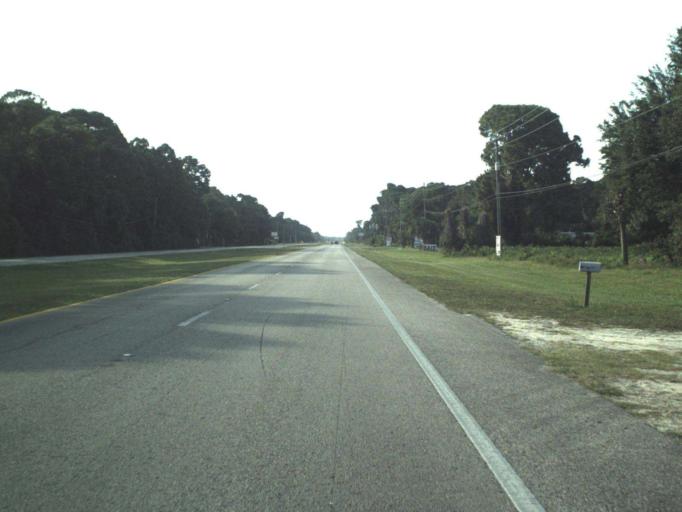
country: US
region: Florida
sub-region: Volusia County
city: Oak Hill
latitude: 28.9149
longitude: -80.8690
